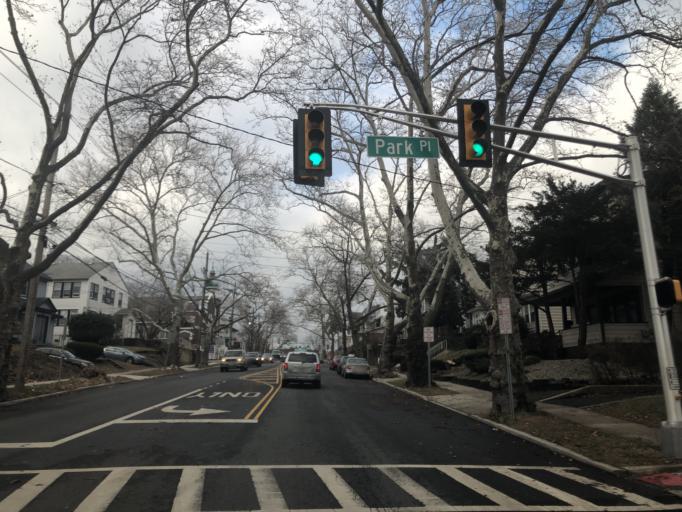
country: US
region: New Jersey
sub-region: Essex County
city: Irvington
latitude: 40.7226
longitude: -74.2364
